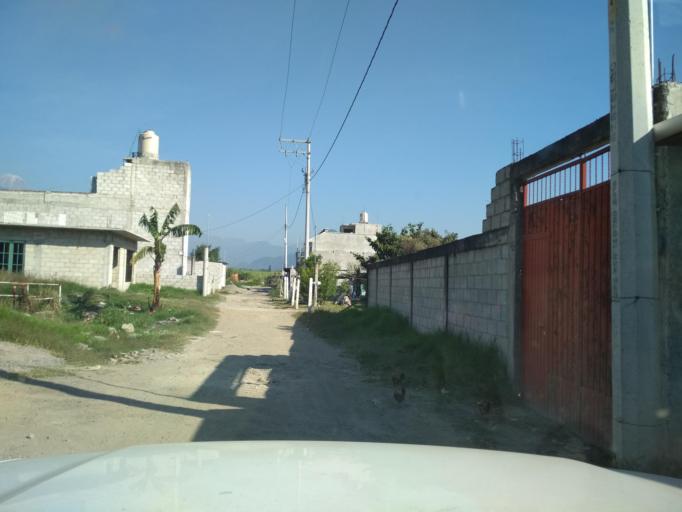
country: MX
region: Veracruz
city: Jalapilla
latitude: 18.8181
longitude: -97.0761
